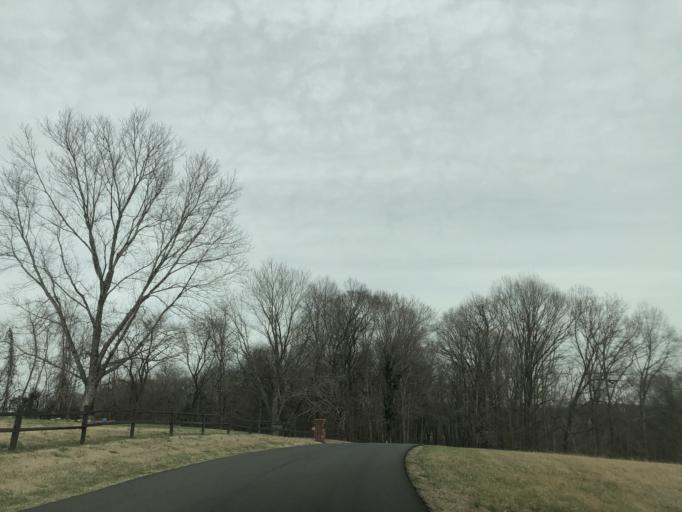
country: US
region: Tennessee
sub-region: Robertson County
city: Greenbrier
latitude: 36.4814
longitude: -86.7955
